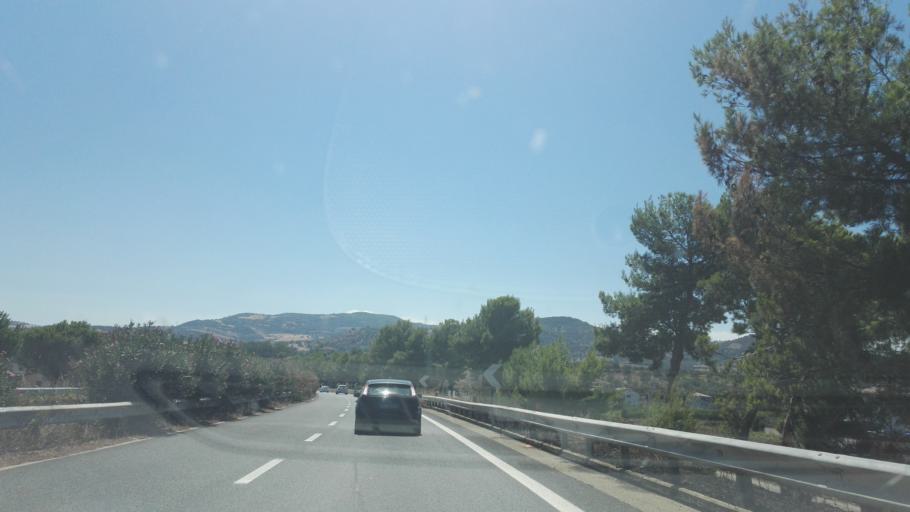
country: IT
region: Calabria
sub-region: Provincia di Cosenza
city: Rocca Imperiale Marina
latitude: 40.1036
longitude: 16.6125
